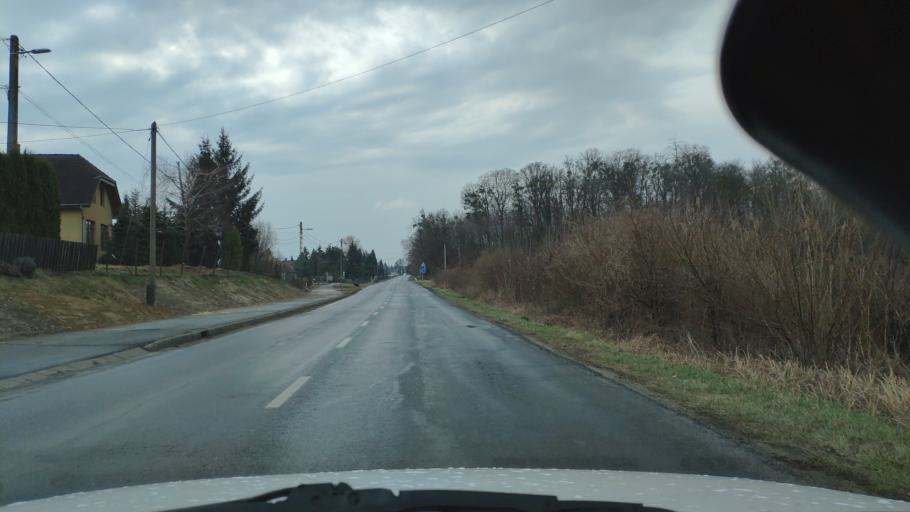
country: HU
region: Zala
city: Nagykanizsa
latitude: 46.4170
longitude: 16.9848
